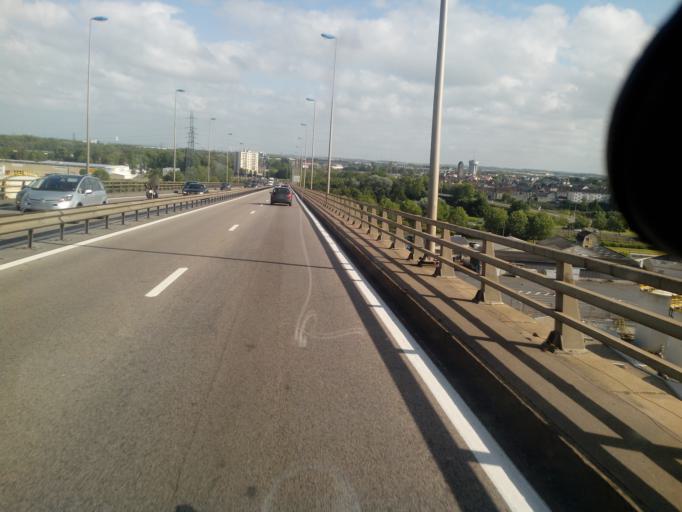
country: FR
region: Lower Normandy
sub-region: Departement du Calvados
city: Mondeville
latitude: 49.1841
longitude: -0.3276
